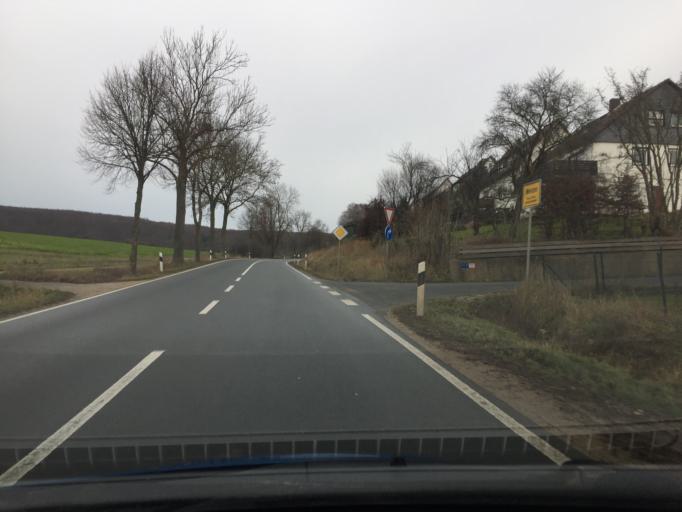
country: DE
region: Lower Saxony
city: Weenzen
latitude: 52.0254
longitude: 9.6749
